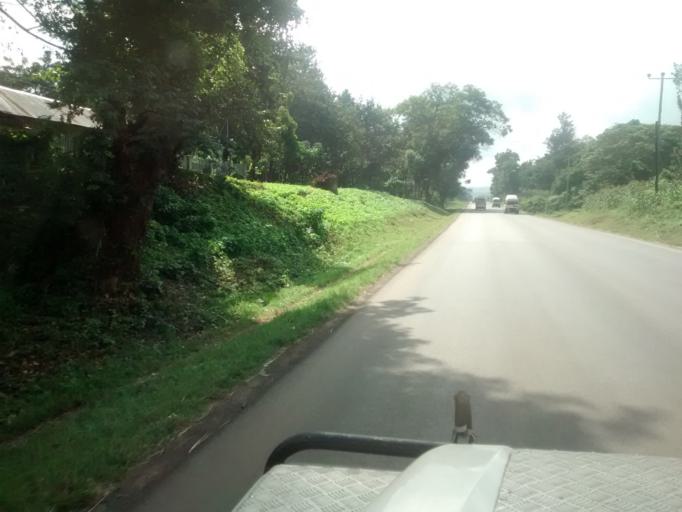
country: TZ
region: Arusha
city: Usa River
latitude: -3.3752
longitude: 36.8349
